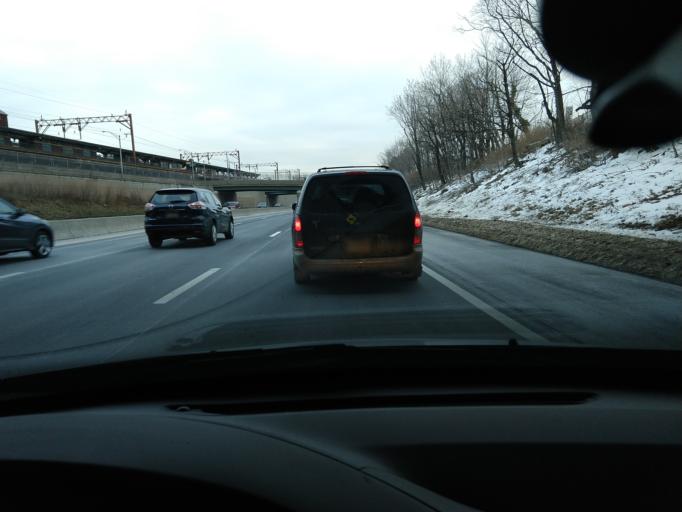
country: US
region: New Jersey
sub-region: Essex County
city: Orange
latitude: 40.7658
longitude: -74.2211
